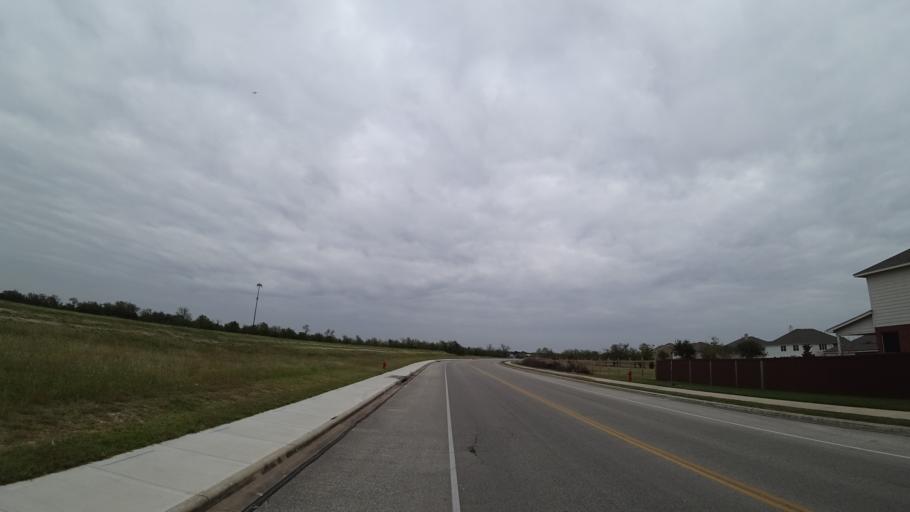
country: US
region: Texas
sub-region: Travis County
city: Pflugerville
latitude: 30.4591
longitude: -97.6275
